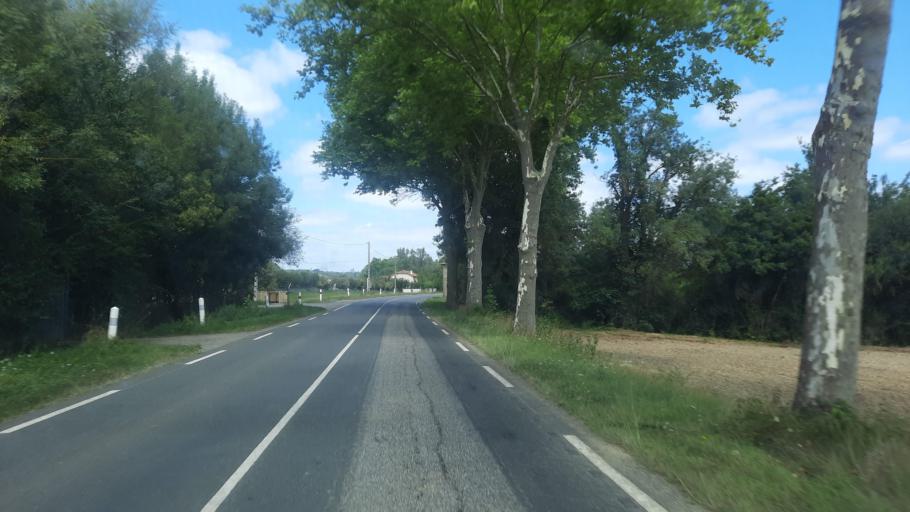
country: FR
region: Midi-Pyrenees
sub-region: Departement de la Haute-Garonne
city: Boulogne-sur-Gesse
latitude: 43.3130
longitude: 0.6808
